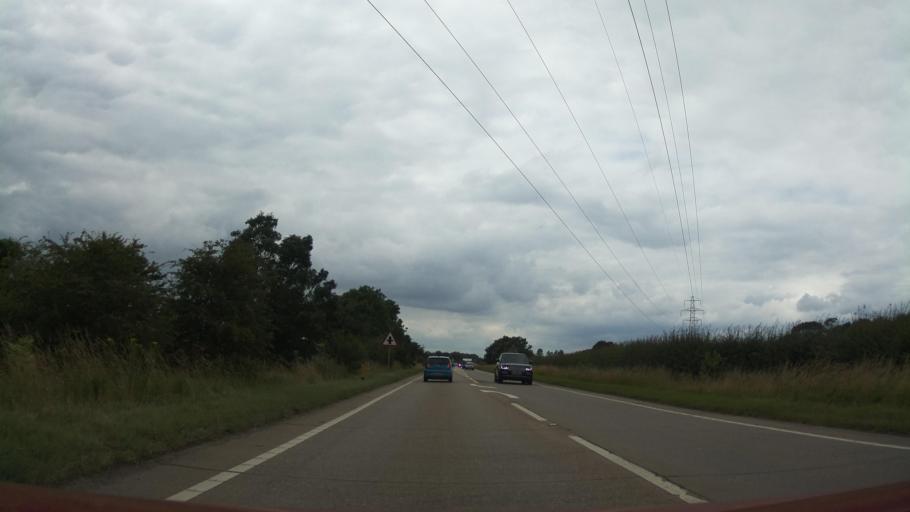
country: GB
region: England
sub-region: Lincolnshire
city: Long Bennington
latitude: 52.9334
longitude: -0.8077
